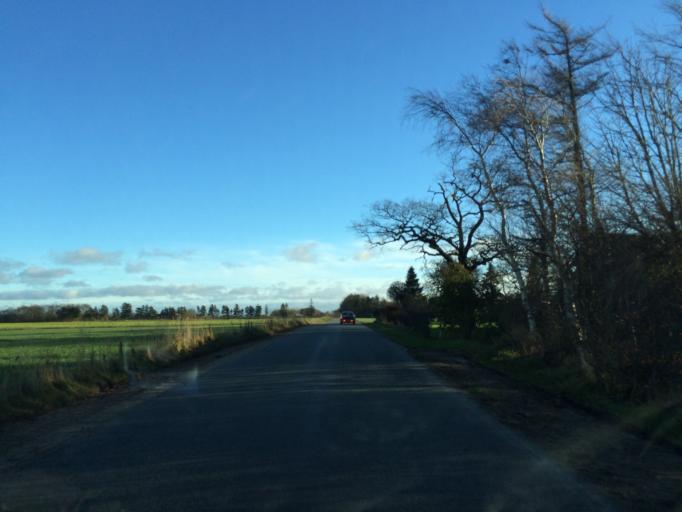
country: DK
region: Central Jutland
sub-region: Herning Kommune
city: Kibaek
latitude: 56.0480
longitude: 8.8020
